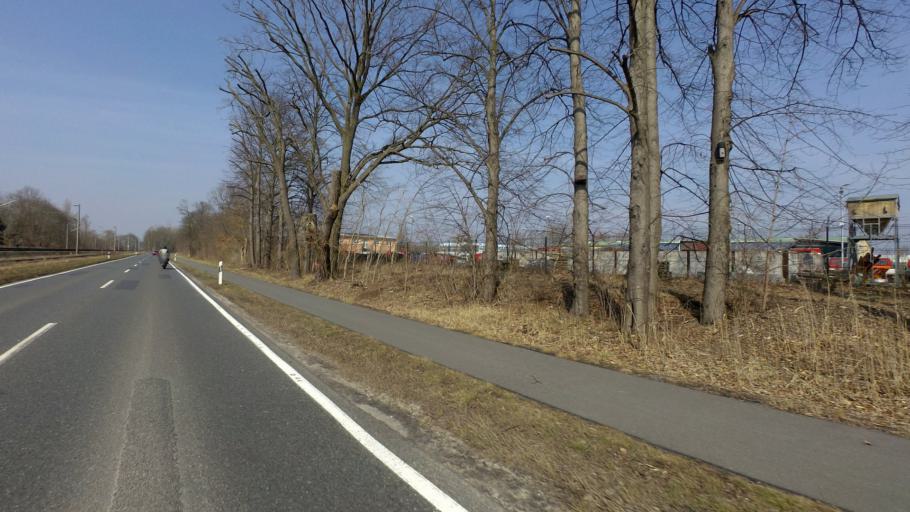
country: DE
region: Brandenburg
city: Werder
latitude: 52.3984
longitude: 12.9115
